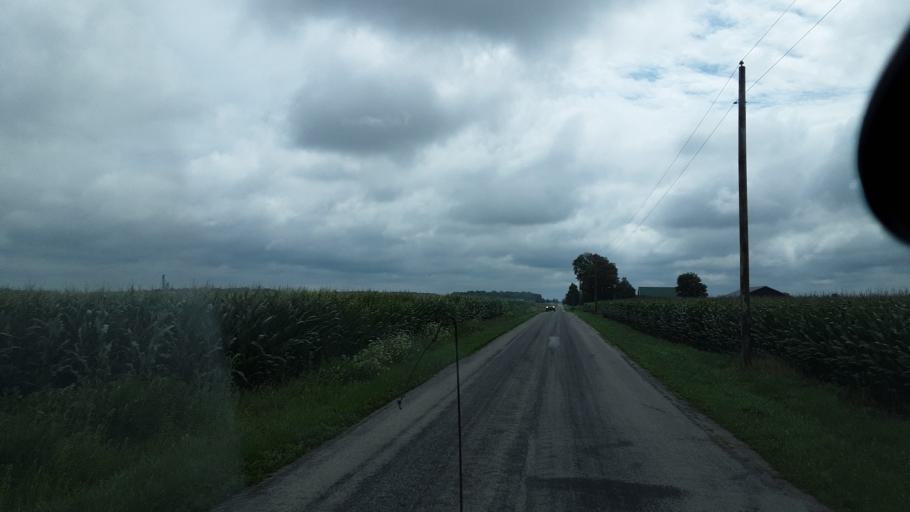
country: US
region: Indiana
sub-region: Wells County
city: Ossian
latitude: 40.8522
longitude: -85.0941
